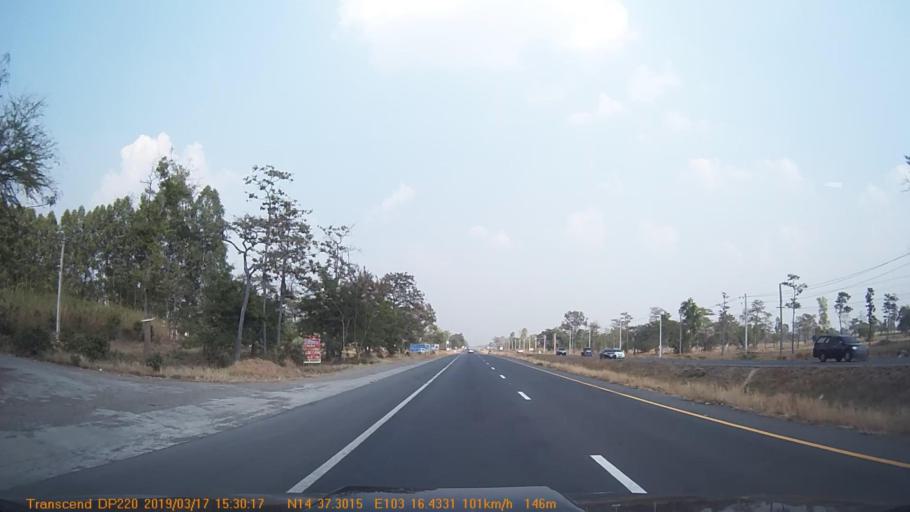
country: TH
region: Surin
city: Prasat
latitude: 14.6216
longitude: 103.2744
